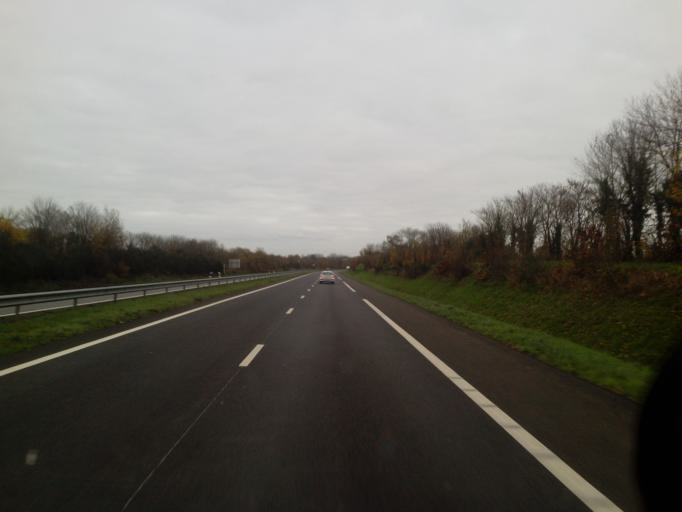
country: FR
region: Pays de la Loire
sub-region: Departement de Maine-et-Loire
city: Saint-Andre-de-la-Marche
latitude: 47.0898
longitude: -0.9912
